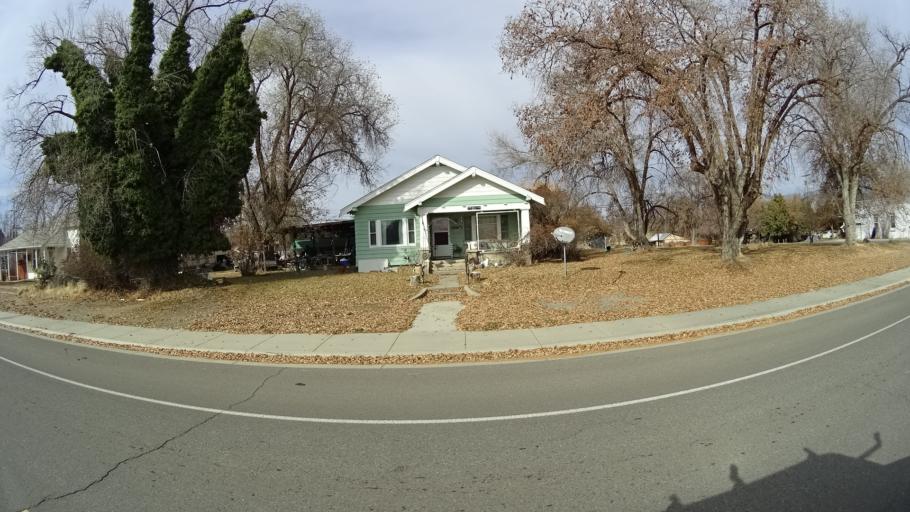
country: US
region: California
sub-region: Siskiyou County
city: Montague
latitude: 41.7302
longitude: -122.5261
